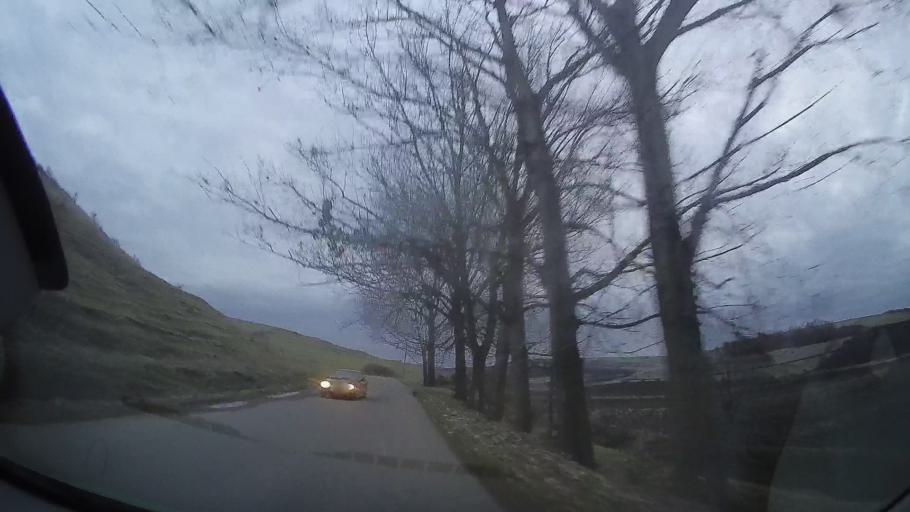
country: RO
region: Cluj
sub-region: Comuna Caianu
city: Vaida-Camaras
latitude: 46.8191
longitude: 23.9358
